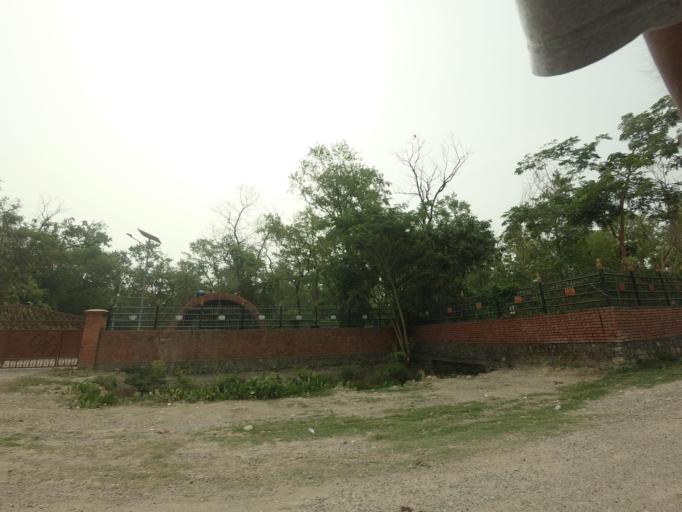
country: IN
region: Uttar Pradesh
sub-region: Maharajganj
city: Nautanwa
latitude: 27.4877
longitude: 83.2680
